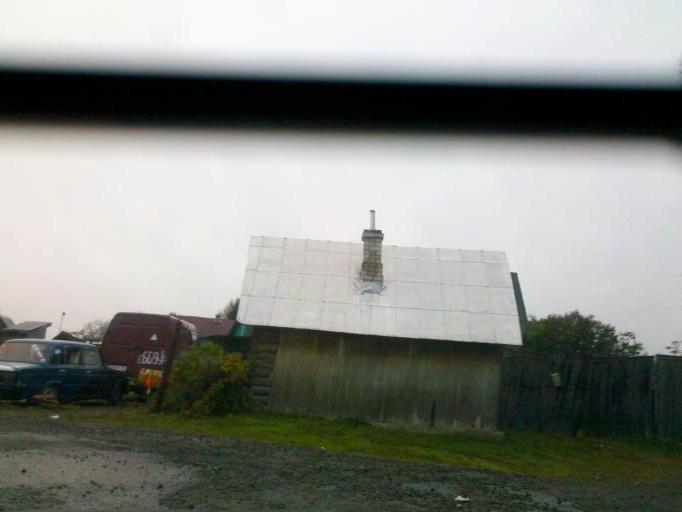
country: RU
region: Republic of Karelia
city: Shuya
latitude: 61.8623
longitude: 34.1579
